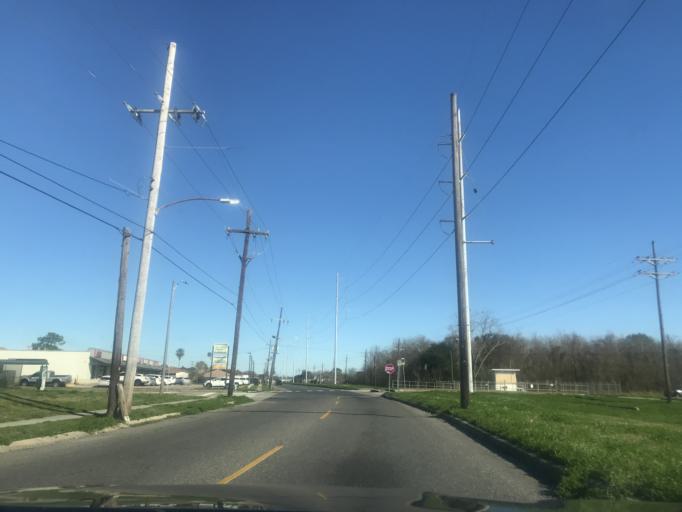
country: US
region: Louisiana
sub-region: Saint Bernard Parish
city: Arabi
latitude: 30.0219
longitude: -90.0003
